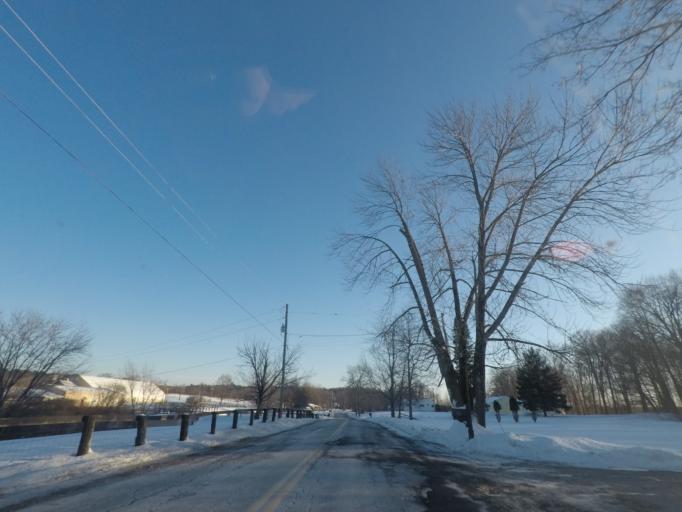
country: US
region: New York
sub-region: Saratoga County
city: Mechanicville
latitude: 42.8824
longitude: -73.6734
